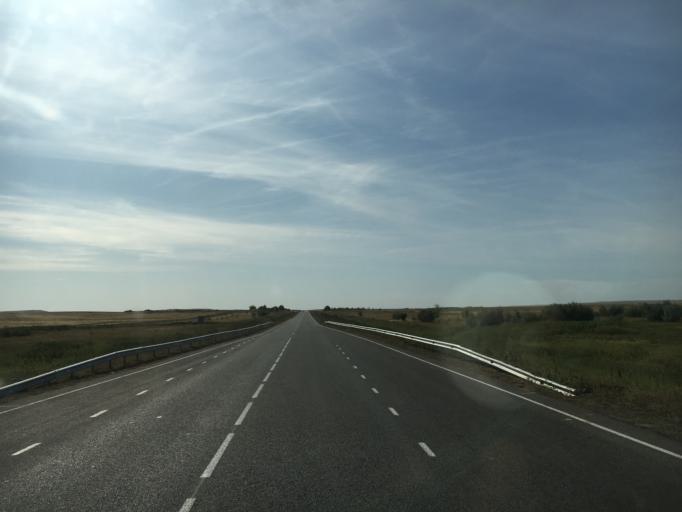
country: KZ
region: Batys Qazaqstan
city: Kamenka
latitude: 51.1071
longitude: 50.4102
